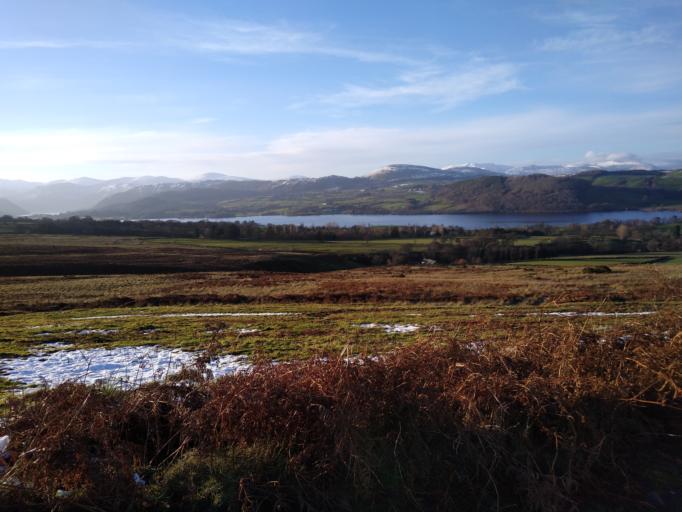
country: GB
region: England
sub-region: Cumbria
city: Penrith
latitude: 54.6007
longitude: -2.8066
